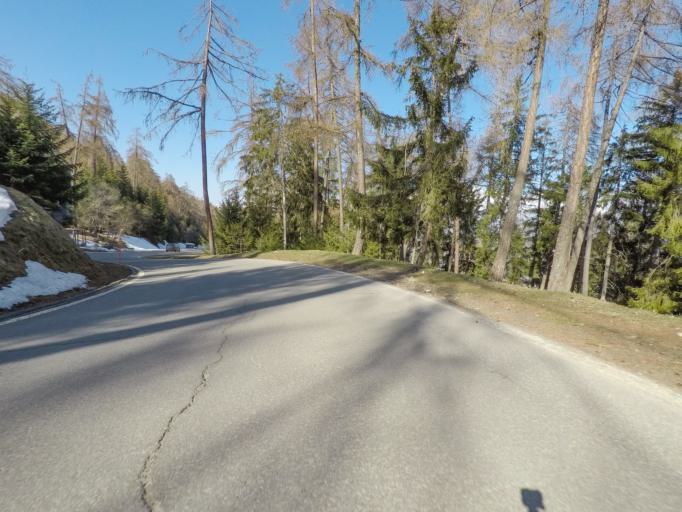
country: CH
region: Valais
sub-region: Sion District
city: Sitten
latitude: 46.1964
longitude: 7.3530
